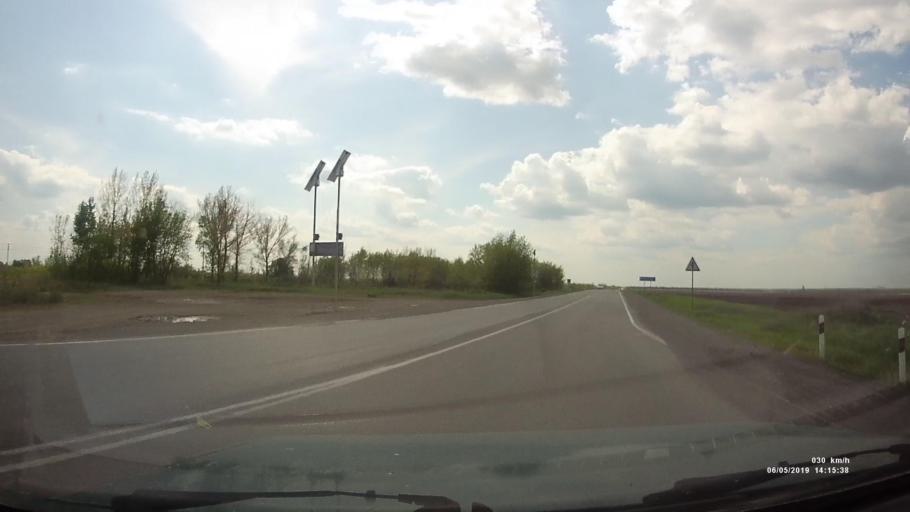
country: RU
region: Rostov
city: Kamenolomni
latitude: 47.6354
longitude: 40.3014
